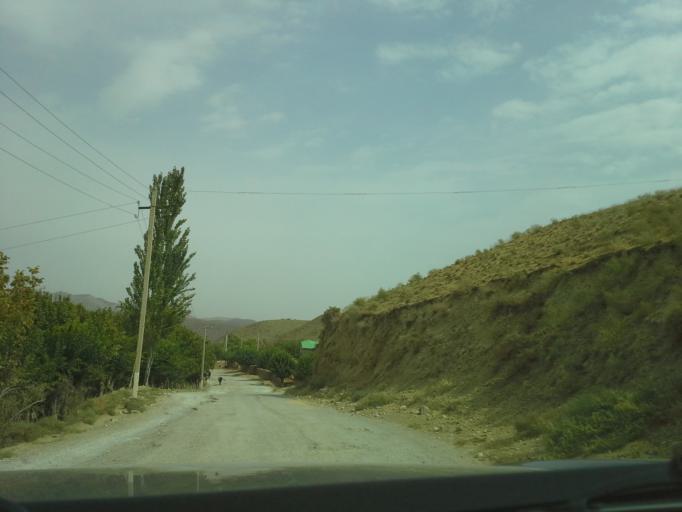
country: UZ
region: Qashqadaryo
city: Qorashina
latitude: 37.9231
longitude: 66.4900
